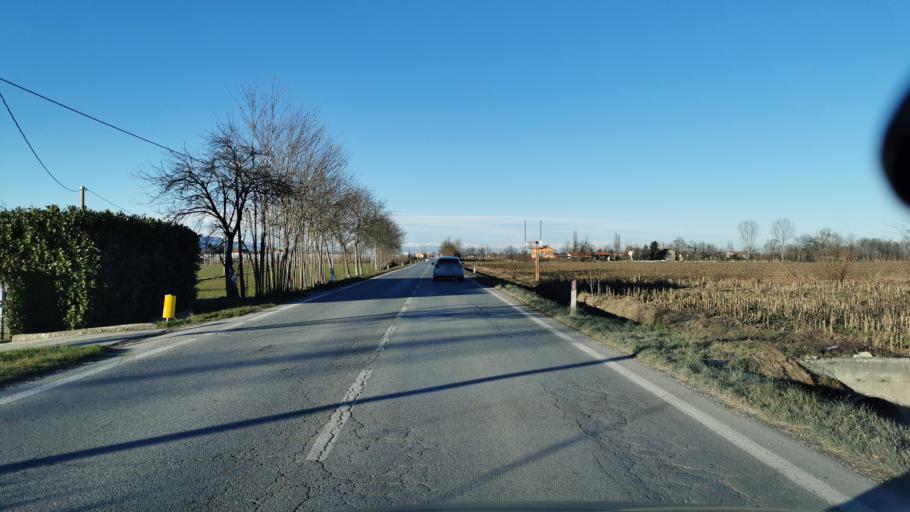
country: IT
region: Piedmont
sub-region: Provincia di Cuneo
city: Roata Rossi
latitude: 44.4302
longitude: 7.5446
